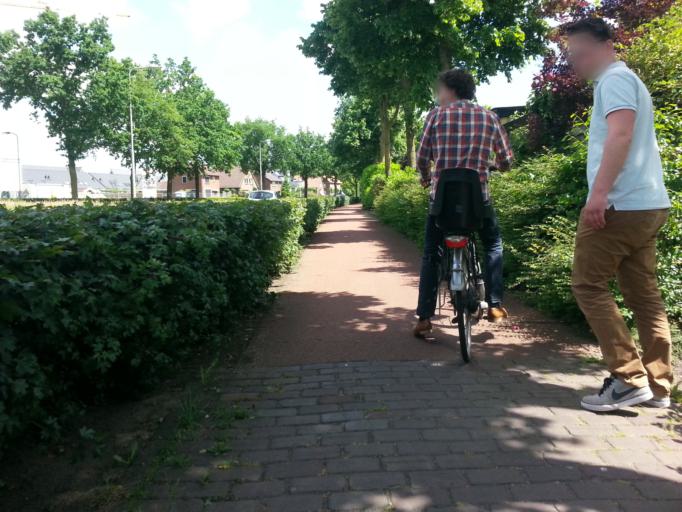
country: NL
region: Gelderland
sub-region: Gemeente Barneveld
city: Barneveld
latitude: 52.1338
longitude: 5.5915
